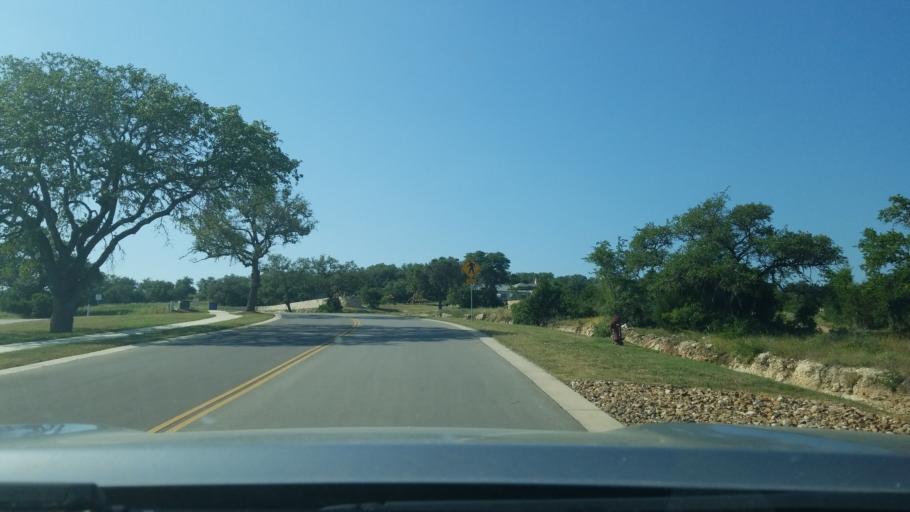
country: US
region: Texas
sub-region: Comal County
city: Bulverde
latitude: 29.7605
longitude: -98.4222
